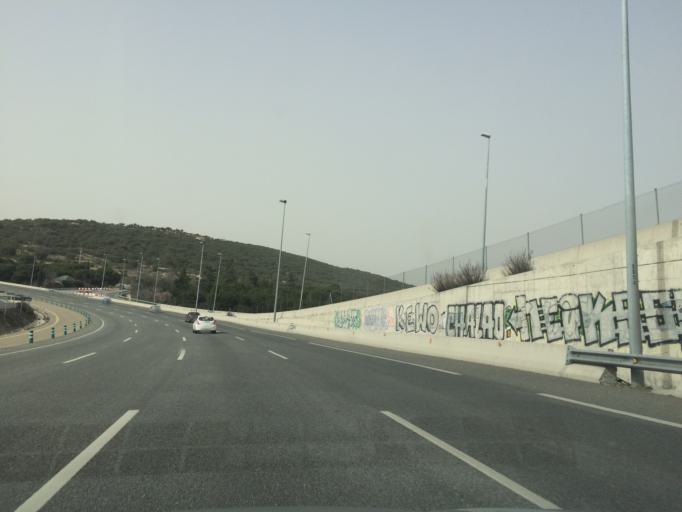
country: ES
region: Madrid
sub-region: Provincia de Madrid
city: Torrelodones
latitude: 40.5954
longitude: -3.9527
